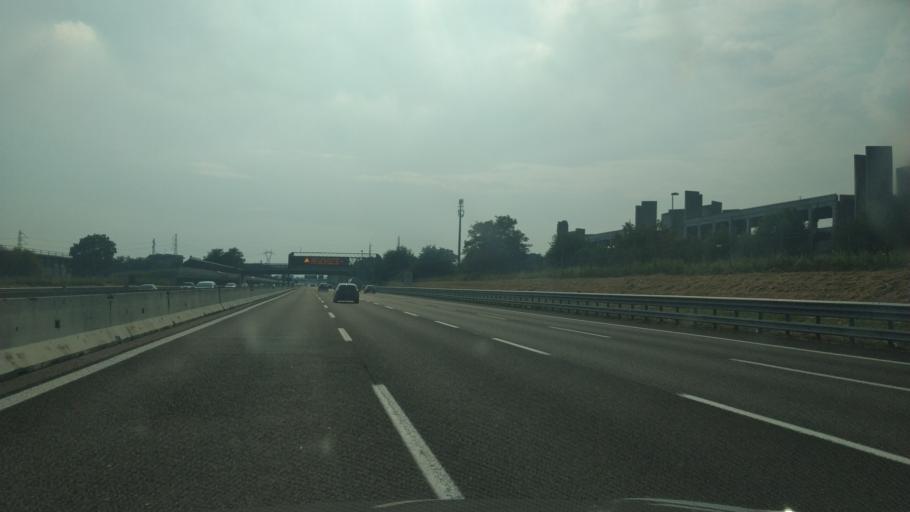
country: IT
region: Lombardy
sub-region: Provincia di Monza e Brianza
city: Brugherio
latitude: 45.5598
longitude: 9.2907
